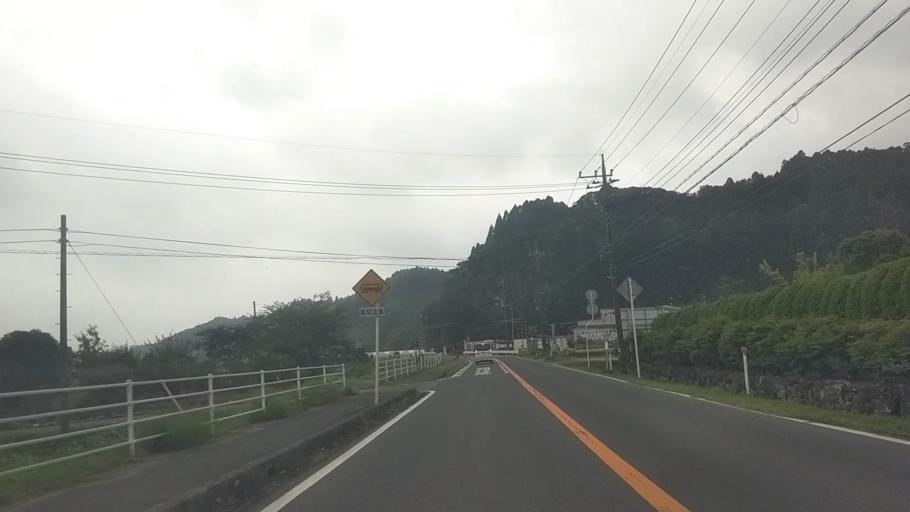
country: JP
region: Chiba
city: Ohara
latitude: 35.2789
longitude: 140.3263
